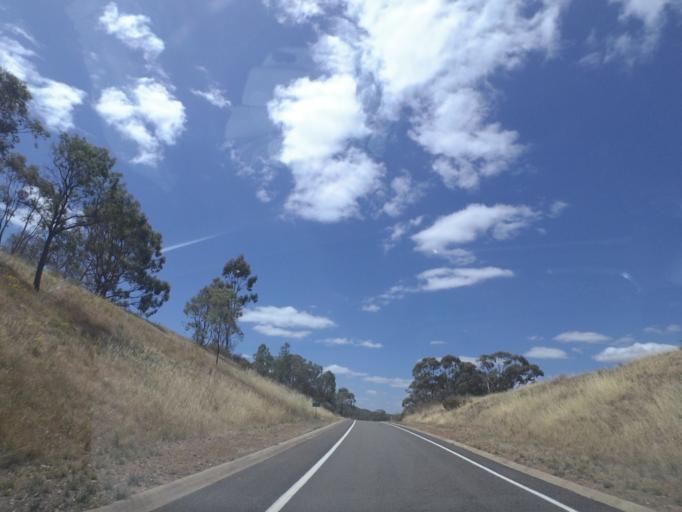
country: AU
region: Victoria
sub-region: Wangaratta
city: Wangaratta
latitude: -36.4675
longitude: 146.2094
